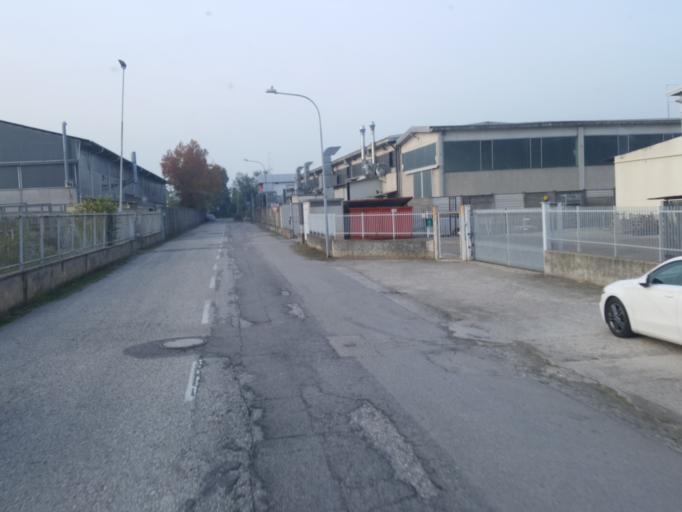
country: IT
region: Veneto
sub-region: Provincia di Verona
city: Zevio
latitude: 45.3702
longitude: 11.0944
